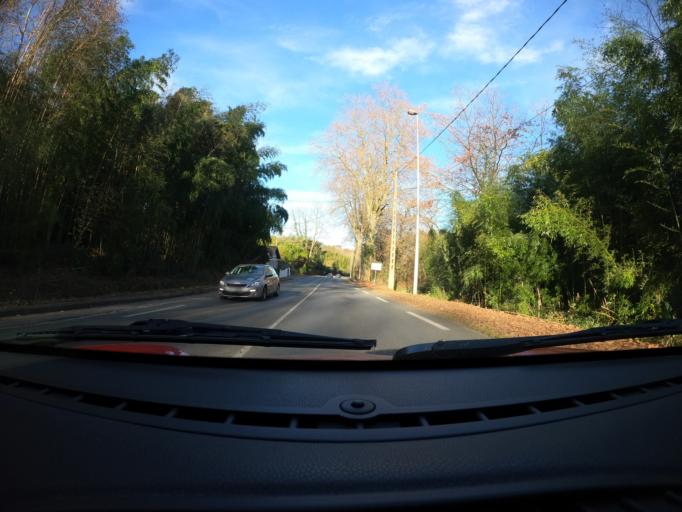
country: FR
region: Aquitaine
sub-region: Departement des Pyrenees-Atlantiques
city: Boucau
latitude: 43.5141
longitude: -1.4672
